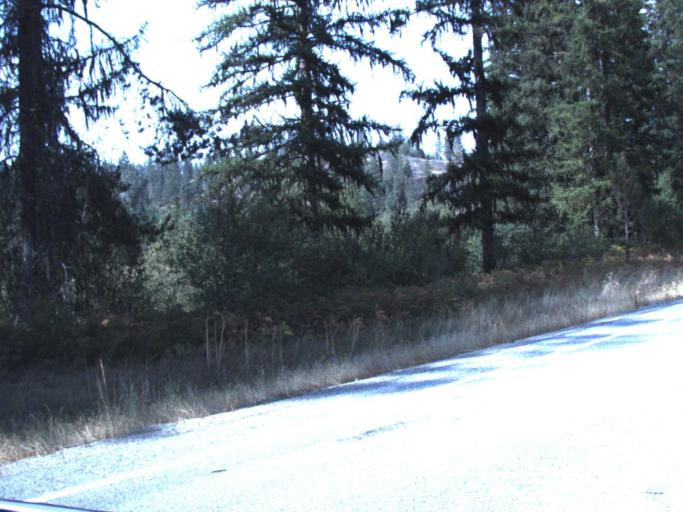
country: US
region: Washington
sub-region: Pend Oreille County
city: Newport
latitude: 48.2024
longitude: -117.2926
